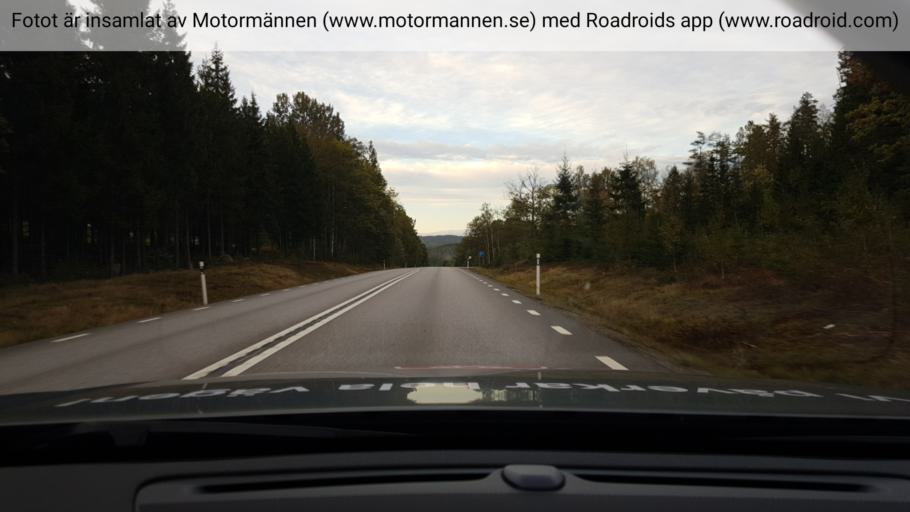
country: SE
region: Vaestra Goetaland
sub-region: Bengtsfors Kommun
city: Dals Langed
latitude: 59.0352
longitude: 12.4228
